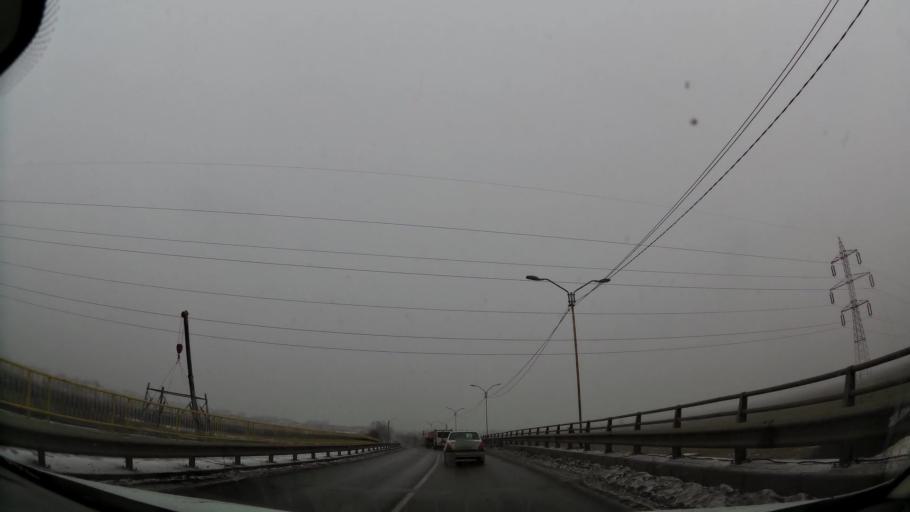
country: RO
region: Dambovita
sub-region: Municipiul Targoviste
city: Targoviste
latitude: 44.9093
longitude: 25.4642
